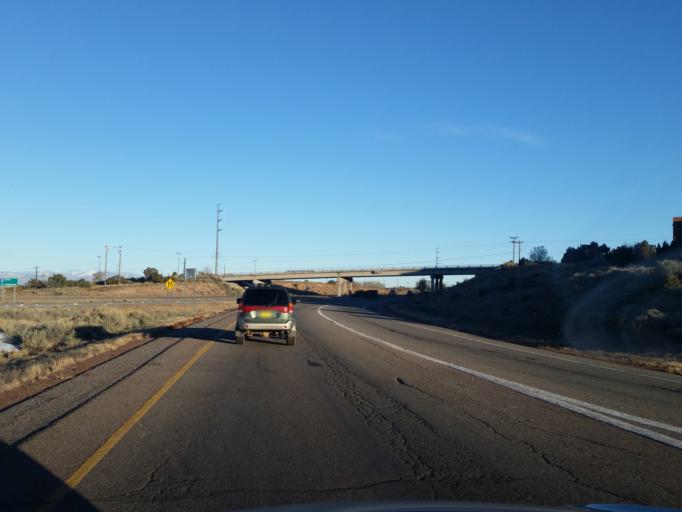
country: US
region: New Mexico
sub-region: Santa Fe County
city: Santa Fe
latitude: 35.6368
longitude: -105.9554
